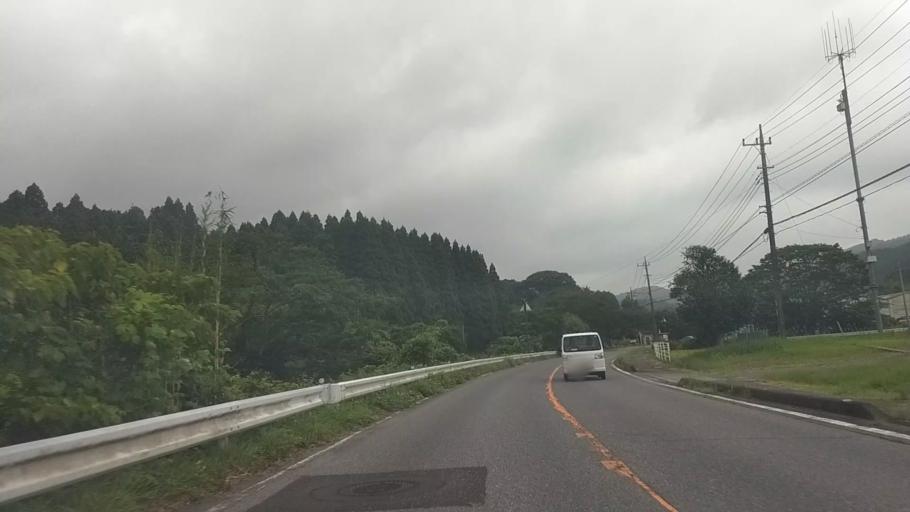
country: JP
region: Chiba
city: Kawaguchi
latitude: 35.1379
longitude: 139.9791
